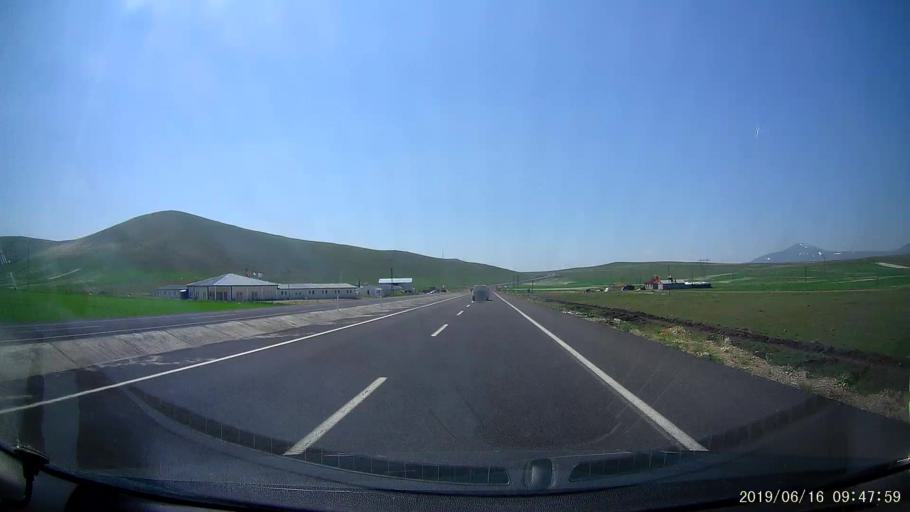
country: TR
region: Kars
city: Digor
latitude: 40.4384
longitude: 43.3499
